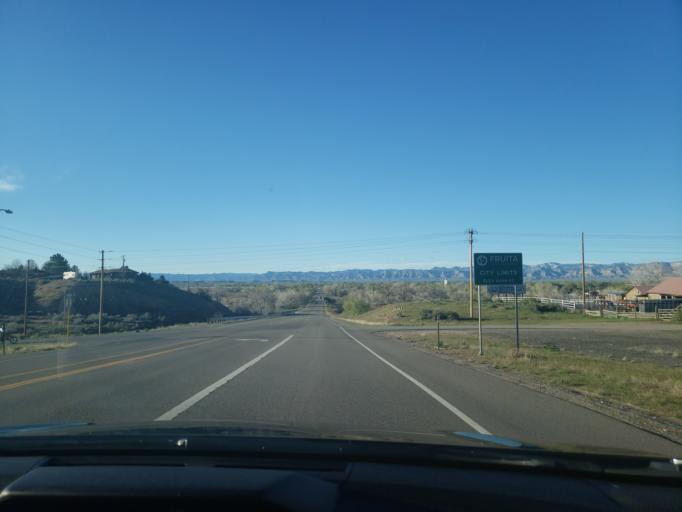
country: US
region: Colorado
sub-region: Mesa County
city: Fruita
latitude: 39.1362
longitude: -108.7383
